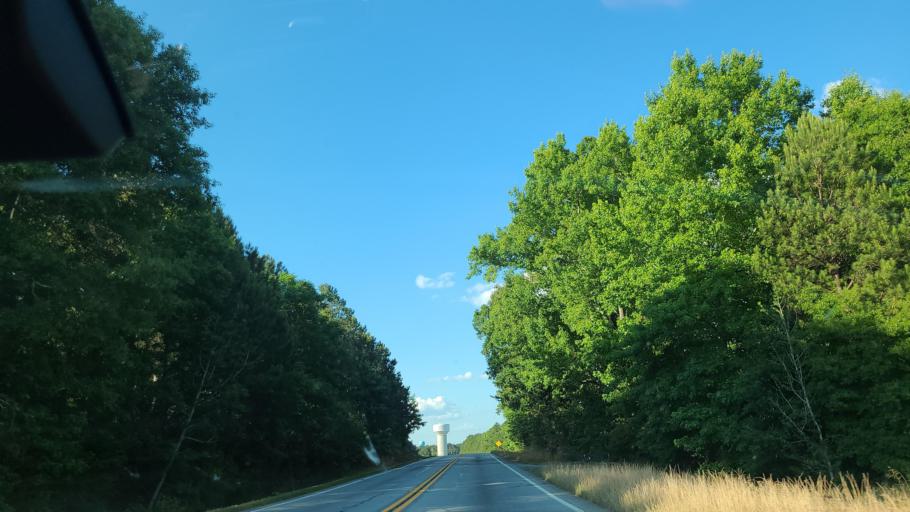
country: US
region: Georgia
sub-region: Oconee County
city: Watkinsville
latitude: 33.8401
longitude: -83.4267
